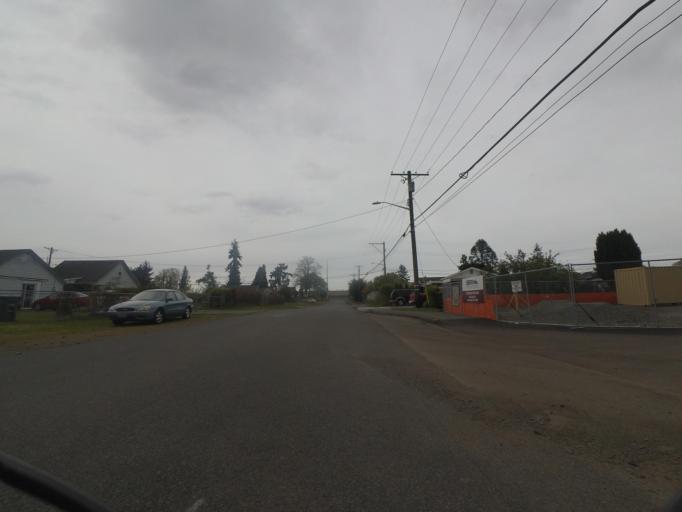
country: US
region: Washington
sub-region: Pierce County
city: Lakewood
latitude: 47.1789
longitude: -122.4810
